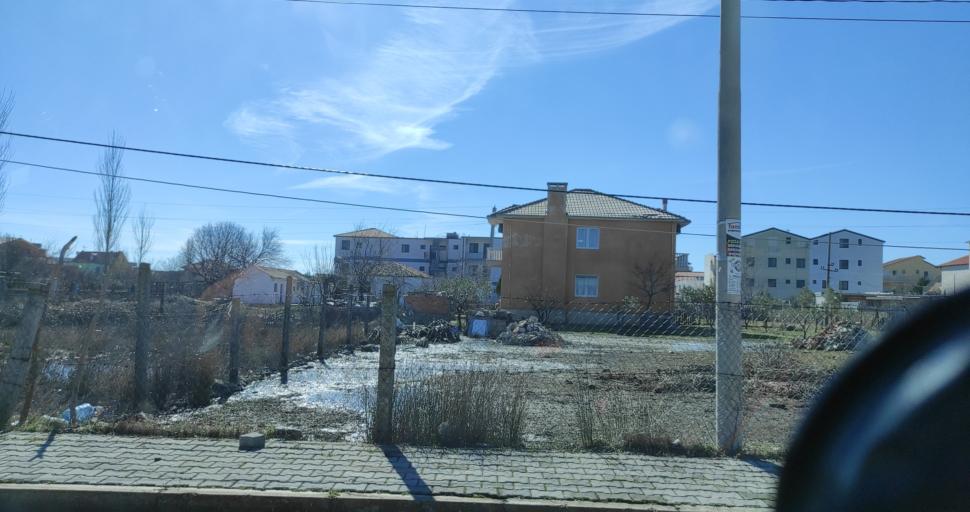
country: AL
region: Shkoder
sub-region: Rrethi i Shkodres
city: Velipoje
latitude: 41.8654
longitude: 19.4364
